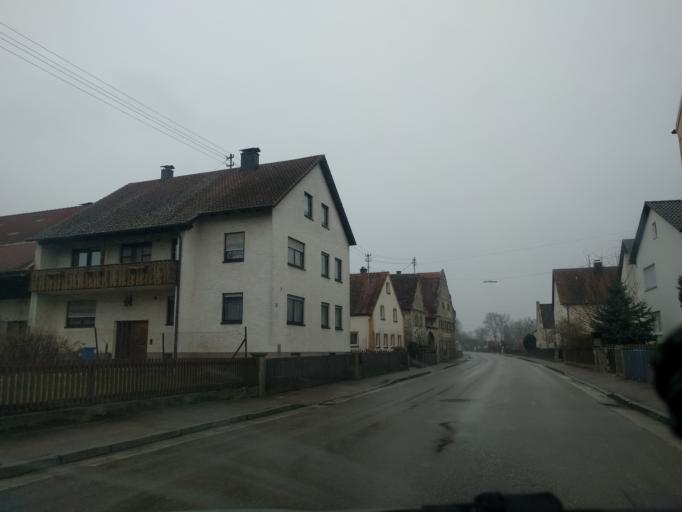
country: DE
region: Bavaria
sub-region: Swabia
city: Donauwoerth
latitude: 48.7031
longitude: 10.7958
